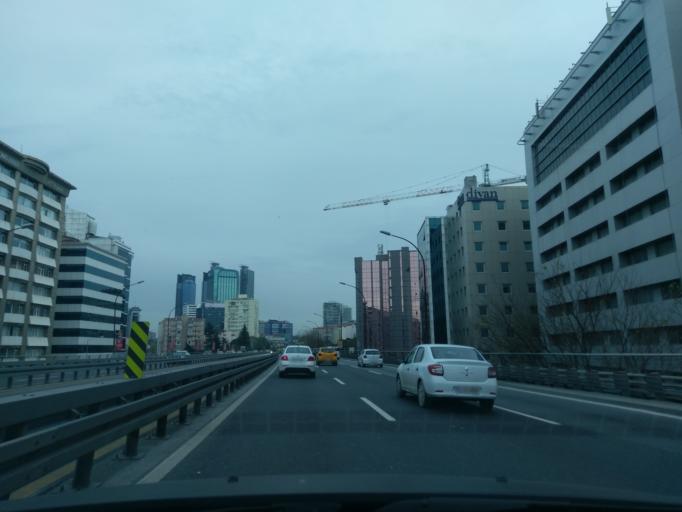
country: TR
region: Istanbul
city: Sisli
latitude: 41.0665
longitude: 29.0016
